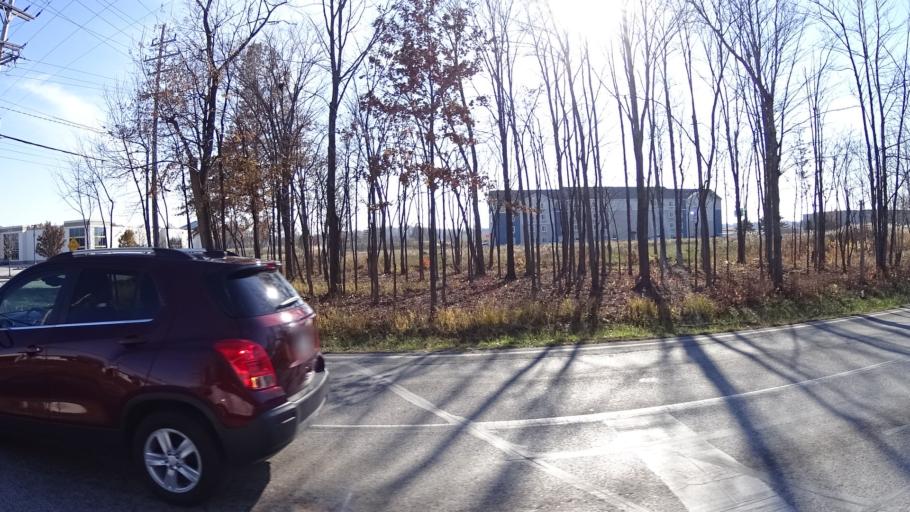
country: US
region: Ohio
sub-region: Lorain County
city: Avon
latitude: 41.4671
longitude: -82.0482
